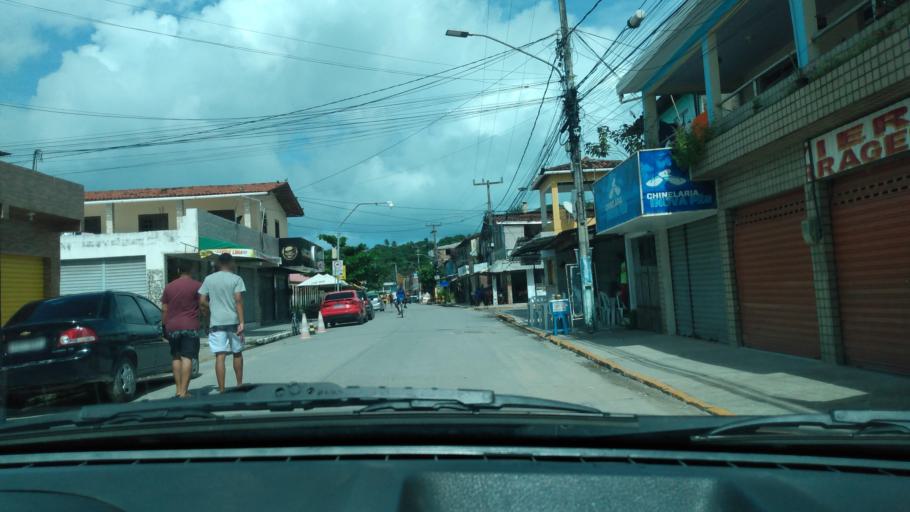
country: BR
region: Pernambuco
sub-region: Cabo De Santo Agostinho
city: Cabo
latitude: -8.3398
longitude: -34.9521
